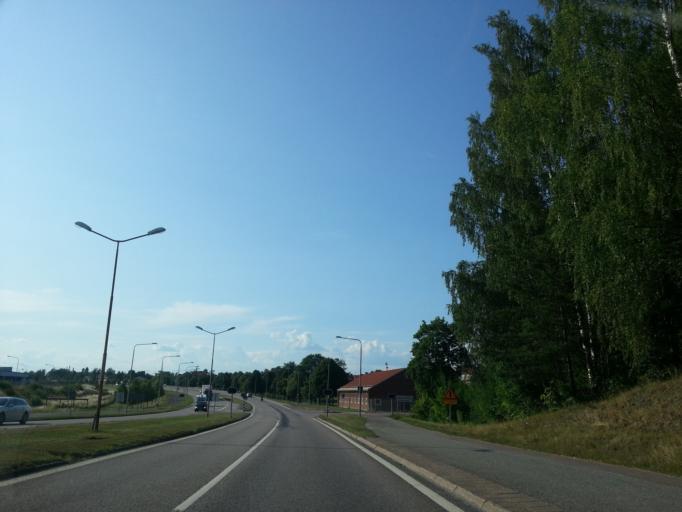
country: SE
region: Vaestmanland
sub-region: Fagersta Kommun
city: Fagersta
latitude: 59.9967
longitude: 15.8068
